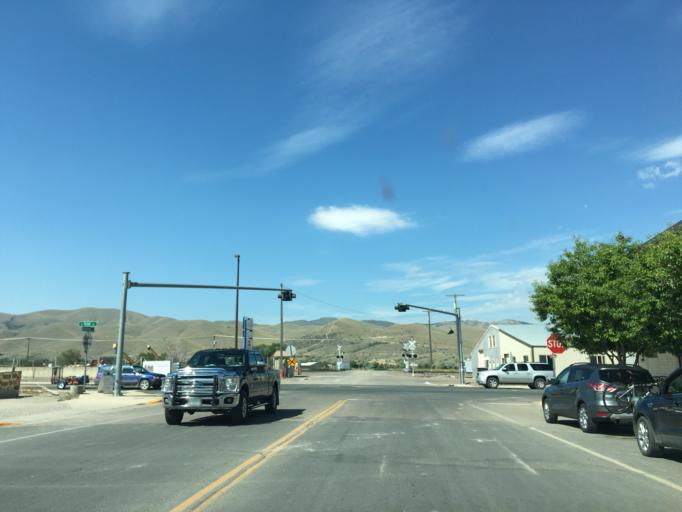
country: US
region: Montana
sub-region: Broadwater County
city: Townsend
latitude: 46.3194
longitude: -111.5209
